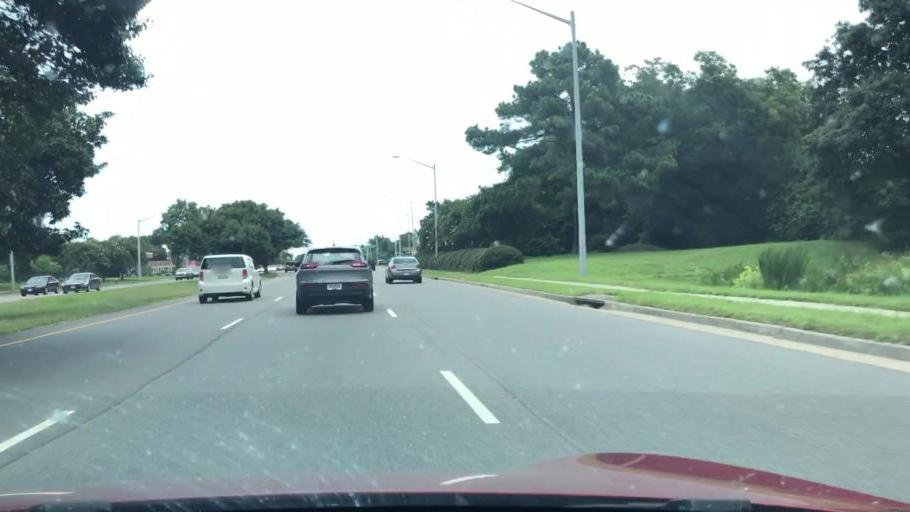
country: US
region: Virginia
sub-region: City of Chesapeake
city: Chesapeake
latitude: 36.8532
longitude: -76.1357
